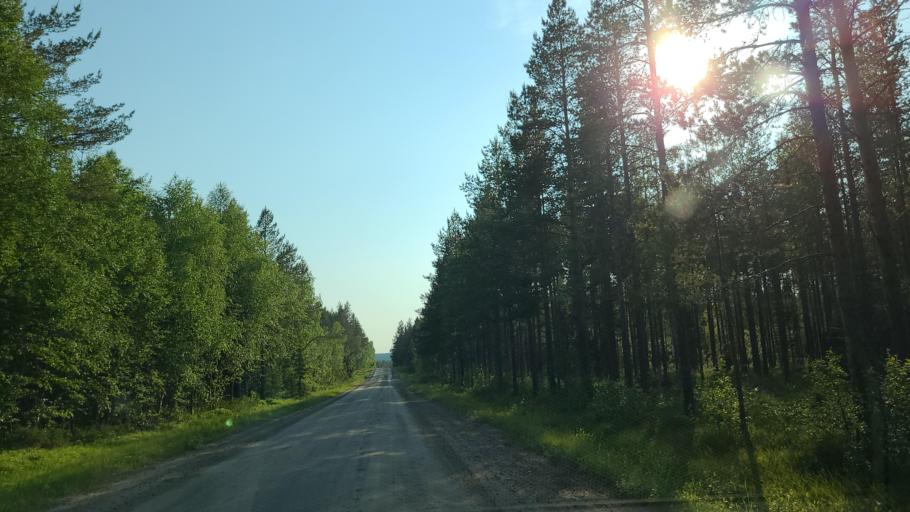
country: SE
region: Vaesterbotten
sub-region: Skelleftea Kommun
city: Burea
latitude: 64.3621
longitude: 21.4374
